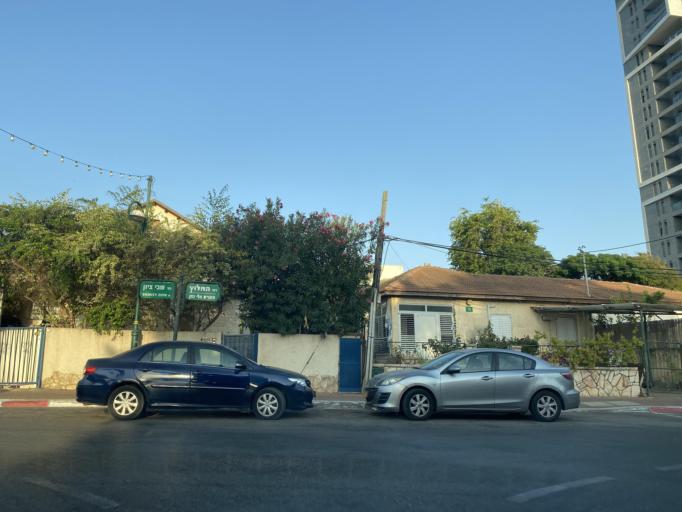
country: IL
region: Tel Aviv
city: Ramat HaSharon
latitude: 32.1338
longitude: 34.8589
